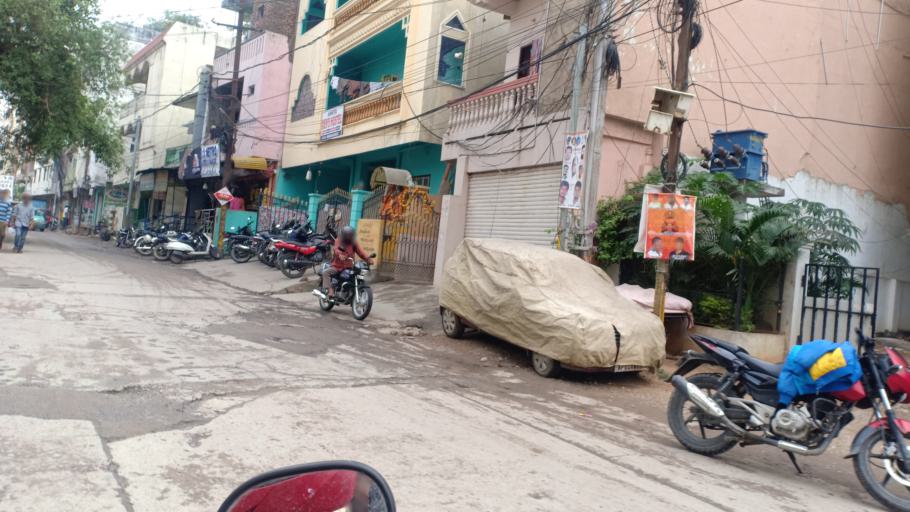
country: IN
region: Telangana
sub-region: Hyderabad
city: Hyderabad
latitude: 17.4325
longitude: 78.4411
